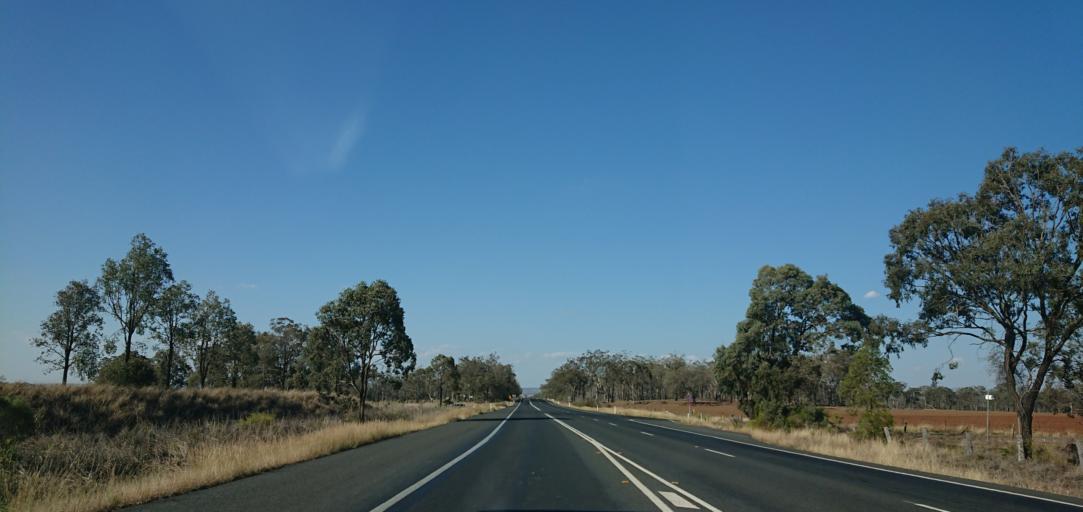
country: AU
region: Queensland
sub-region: Toowoomba
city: Westbrook
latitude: -27.6254
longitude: 151.7600
